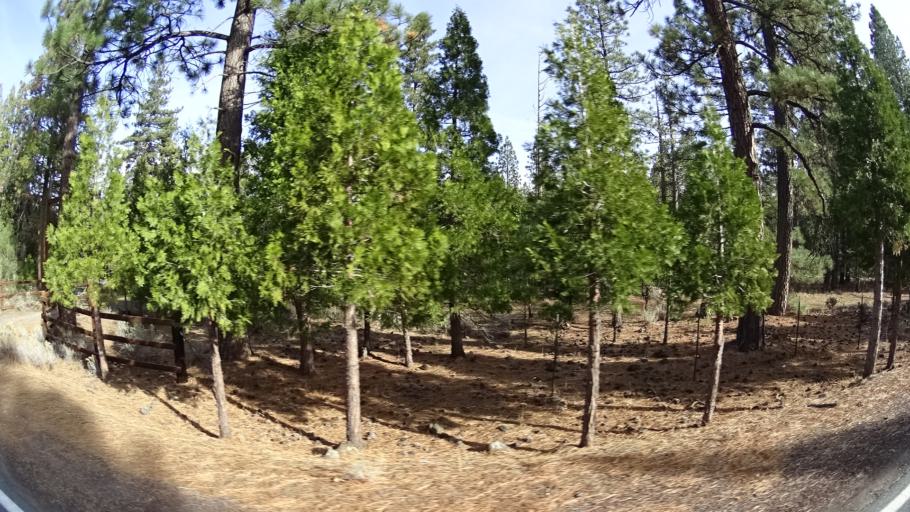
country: US
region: California
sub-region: Siskiyou County
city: Weed
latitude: 41.4126
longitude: -122.4340
